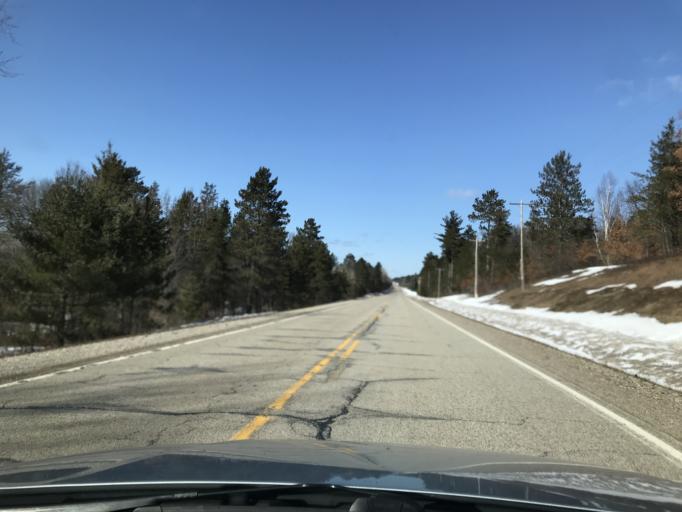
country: US
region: Wisconsin
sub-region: Marinette County
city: Niagara
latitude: 45.3593
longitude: -88.1008
